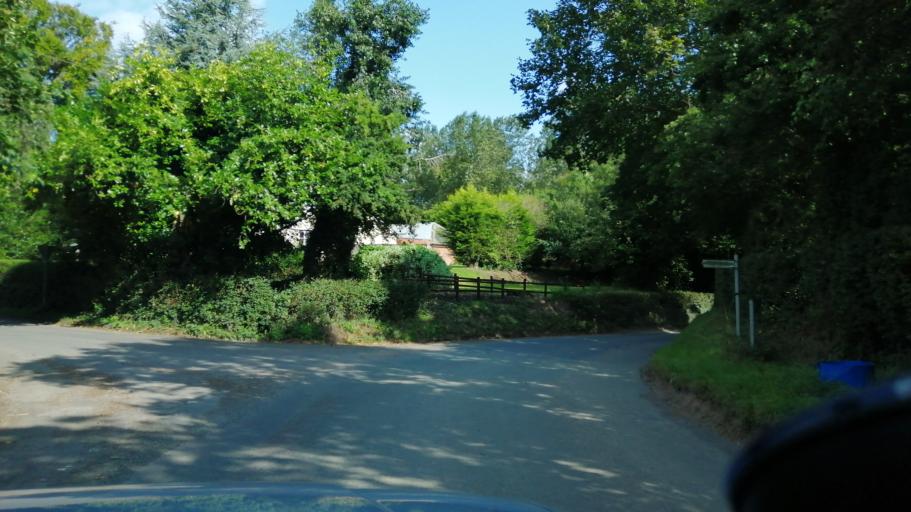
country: GB
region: England
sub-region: Herefordshire
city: Bridge Sollers
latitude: 52.0653
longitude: -2.8643
